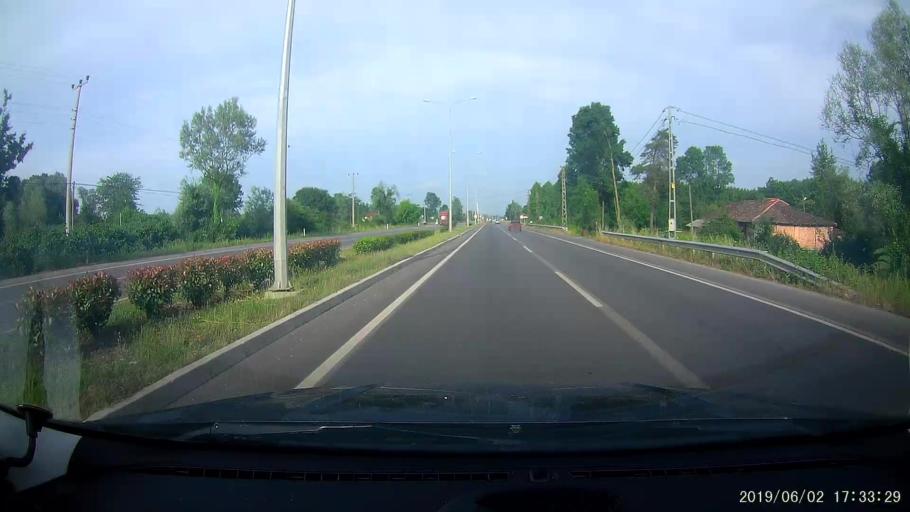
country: TR
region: Samsun
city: Terme
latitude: 41.2208
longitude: 36.8497
